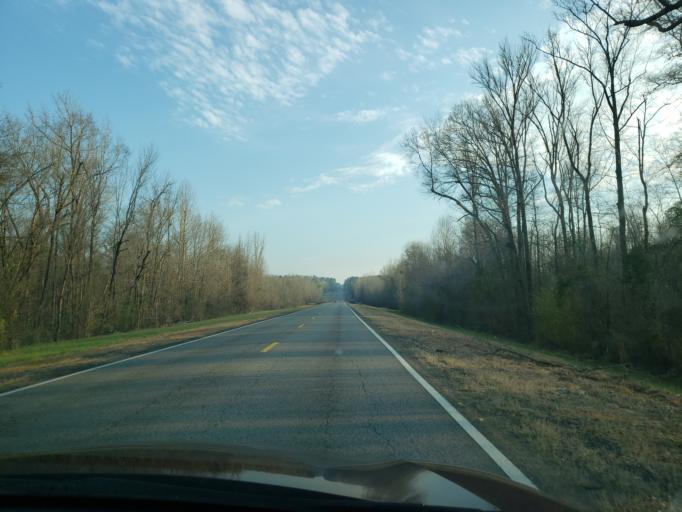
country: US
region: Alabama
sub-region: Hale County
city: Greensboro
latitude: 32.7659
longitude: -87.5854
